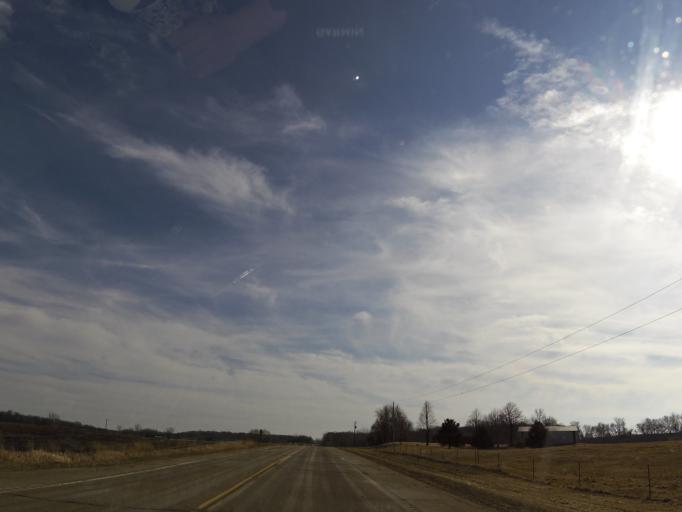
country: US
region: Minnesota
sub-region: Scott County
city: Prior Lake
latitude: 44.6513
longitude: -93.4706
